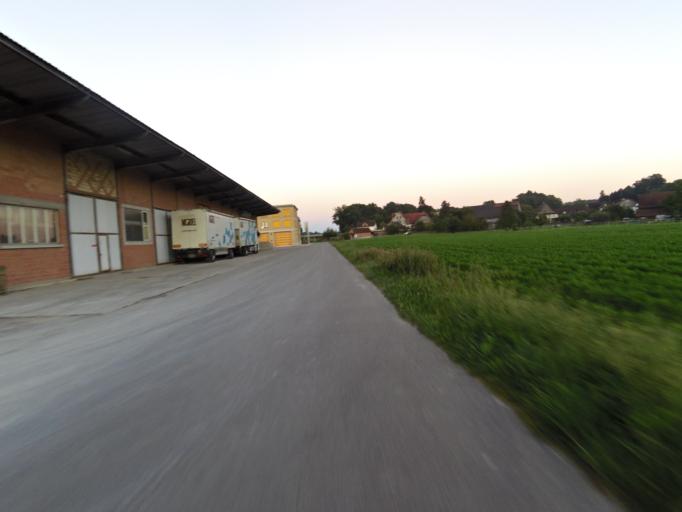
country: CH
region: Thurgau
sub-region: Weinfelden District
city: Maerstetten-Dorf
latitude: 47.5725
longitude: 9.0570
